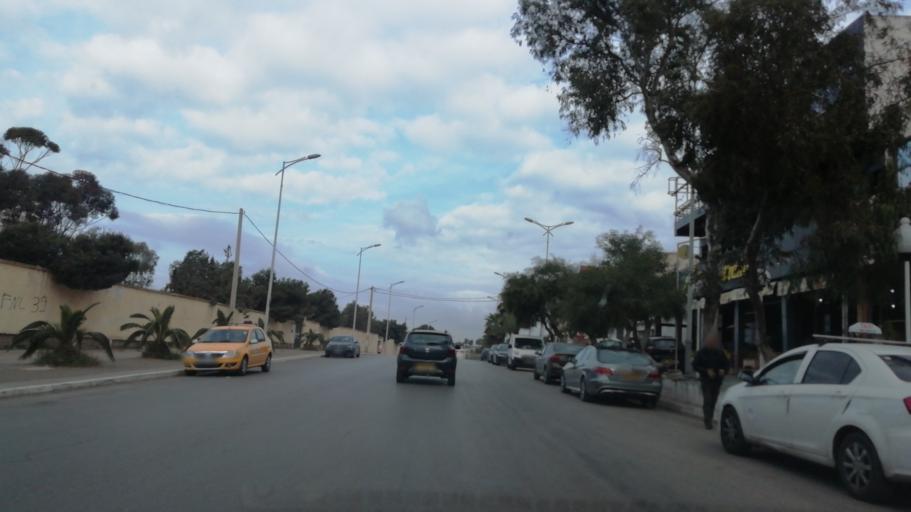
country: DZ
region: Oran
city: Oran
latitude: 35.7119
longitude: -0.6118
